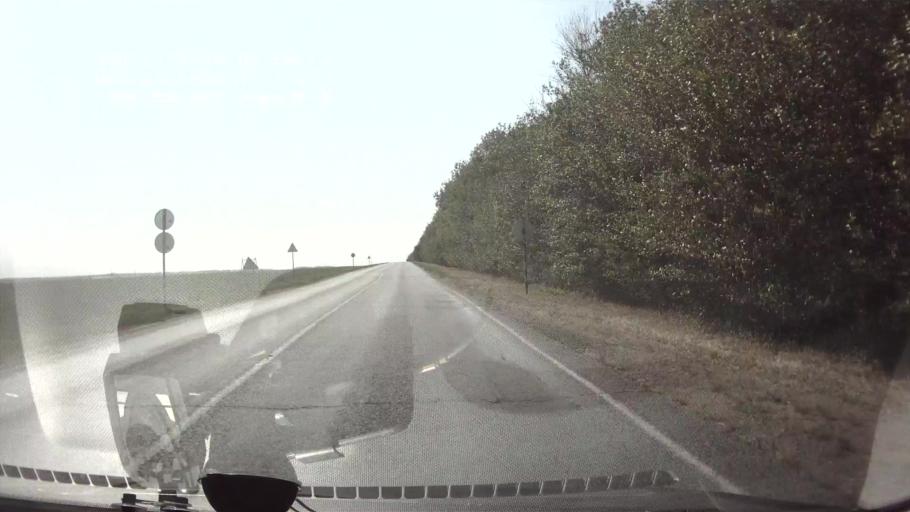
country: RU
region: Krasnodarskiy
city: Dmitriyevskaya
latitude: 45.6722
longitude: 40.7440
